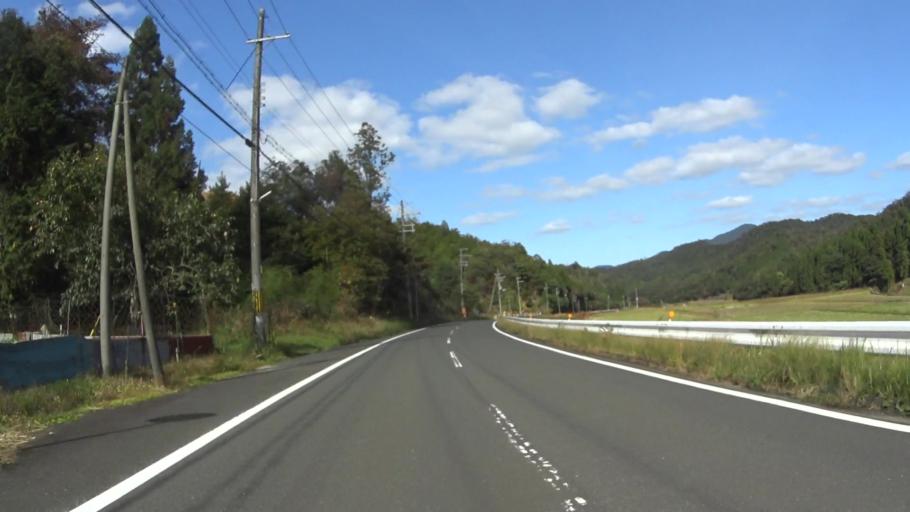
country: JP
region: Hyogo
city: Toyooka
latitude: 35.5526
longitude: 134.9769
